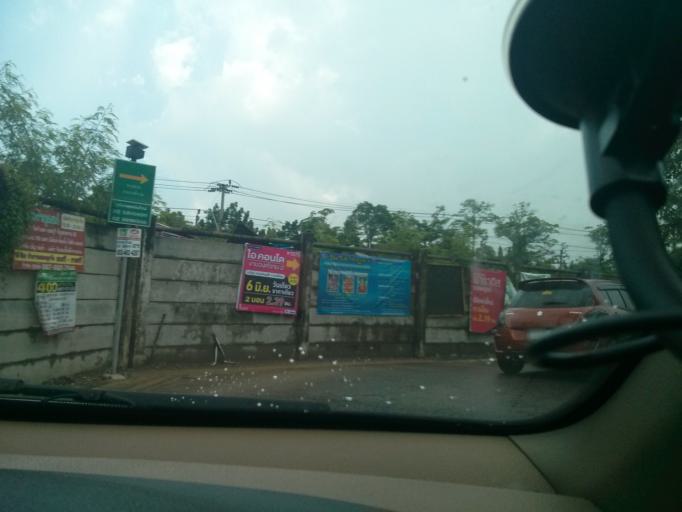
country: TH
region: Nonthaburi
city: Mueang Nonthaburi
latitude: 13.8437
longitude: 100.5221
